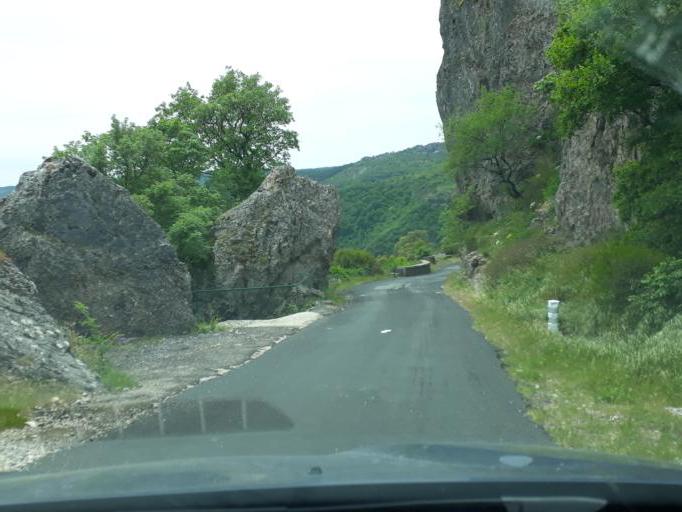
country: FR
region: Languedoc-Roussillon
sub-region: Departement de l'Herault
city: Lodeve
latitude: 43.8061
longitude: 3.2688
